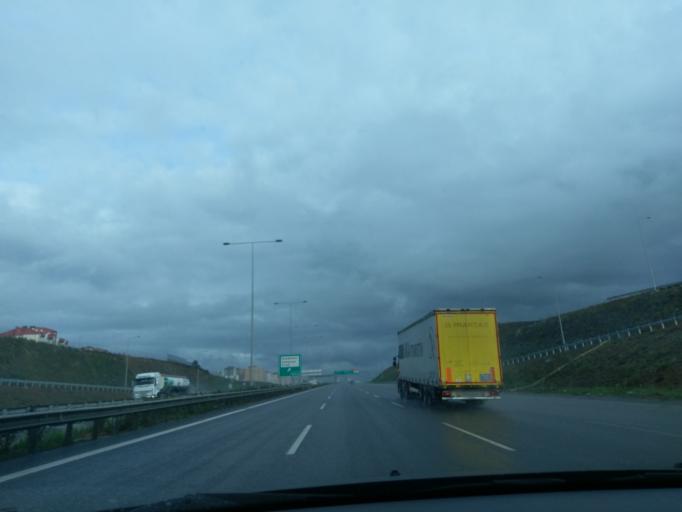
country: TR
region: Istanbul
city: Basaksehir
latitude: 41.0925
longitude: 28.8141
